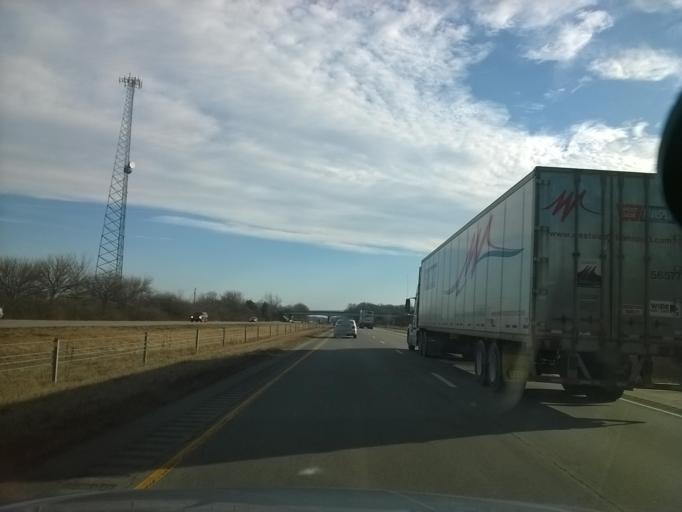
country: US
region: Indiana
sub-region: Johnson County
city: Franklin
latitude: 39.4574
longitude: -86.0003
